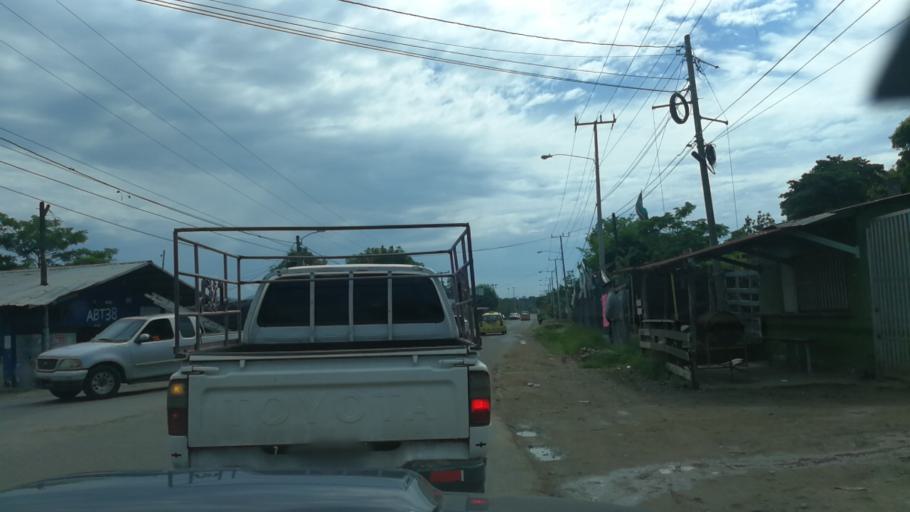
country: PA
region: Panama
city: Paso Blanco
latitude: 9.1186
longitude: -79.2580
